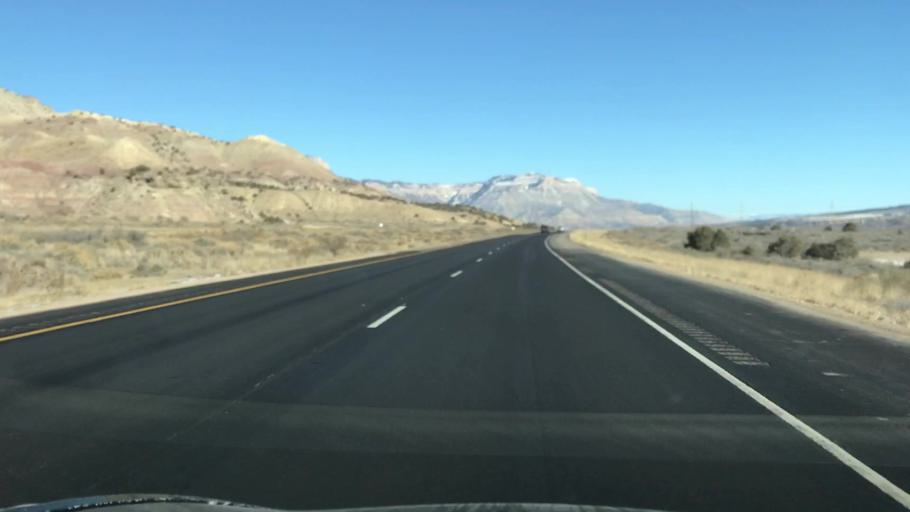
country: US
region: Colorado
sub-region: Garfield County
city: Parachute
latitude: 39.4185
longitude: -108.0896
